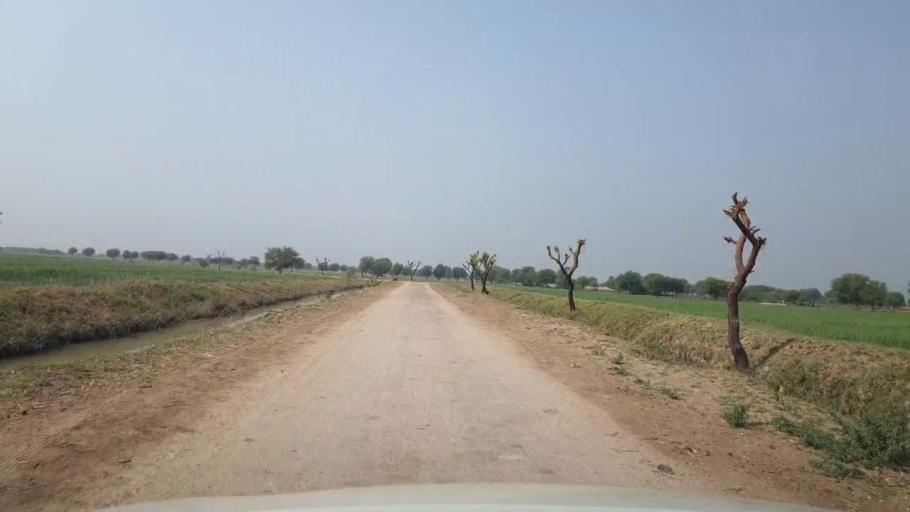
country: PK
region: Sindh
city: Umarkot
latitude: 25.4467
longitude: 69.7096
